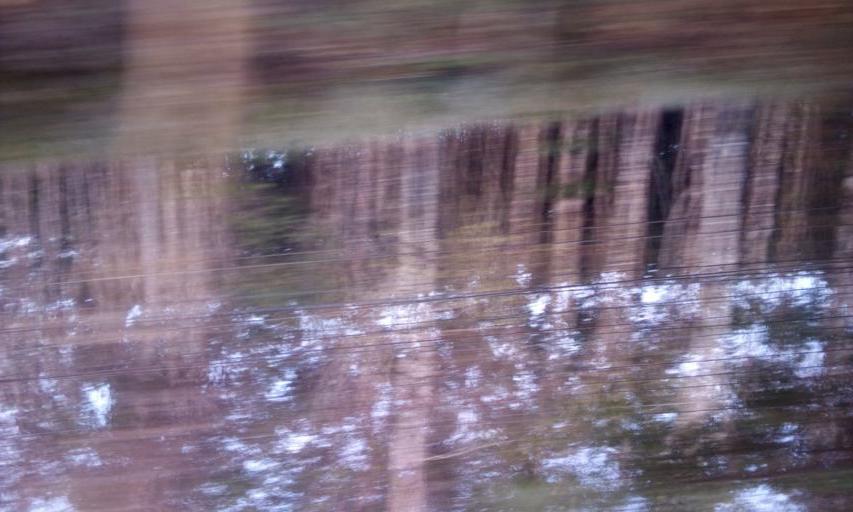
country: TH
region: Trat
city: Khao Saming
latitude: 12.3531
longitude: 102.3809
